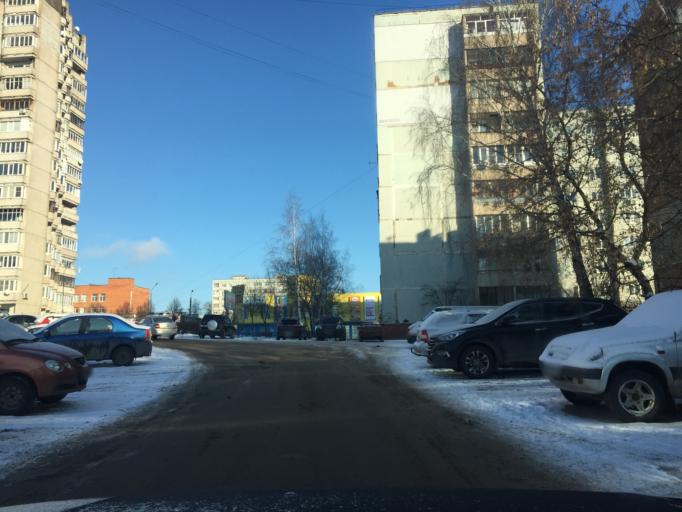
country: RU
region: Tula
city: Tula
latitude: 54.1910
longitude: 37.6863
